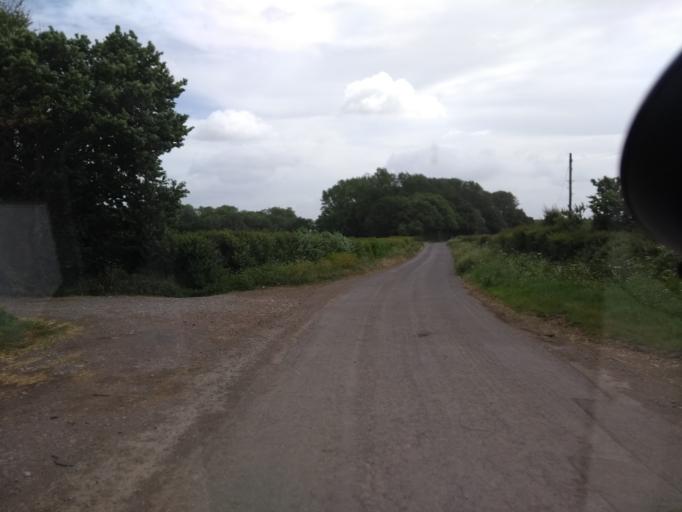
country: GB
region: England
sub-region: Somerset
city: Bishops Lydeard
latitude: 51.1766
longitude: -3.1775
